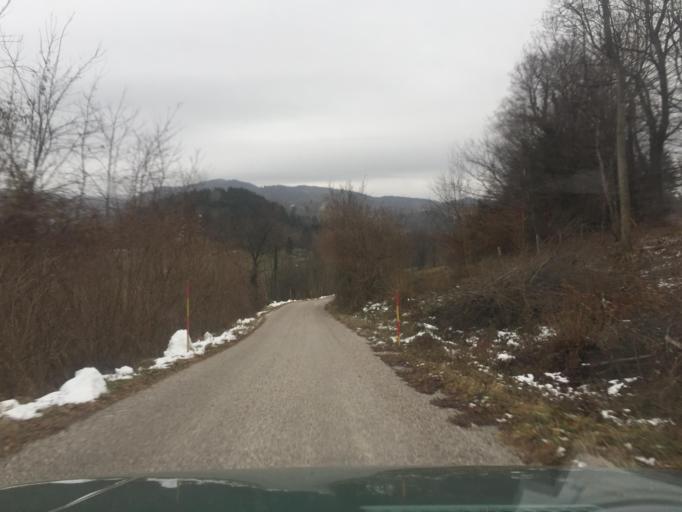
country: SI
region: Kanal
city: Kanal
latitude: 46.0692
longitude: 13.6961
